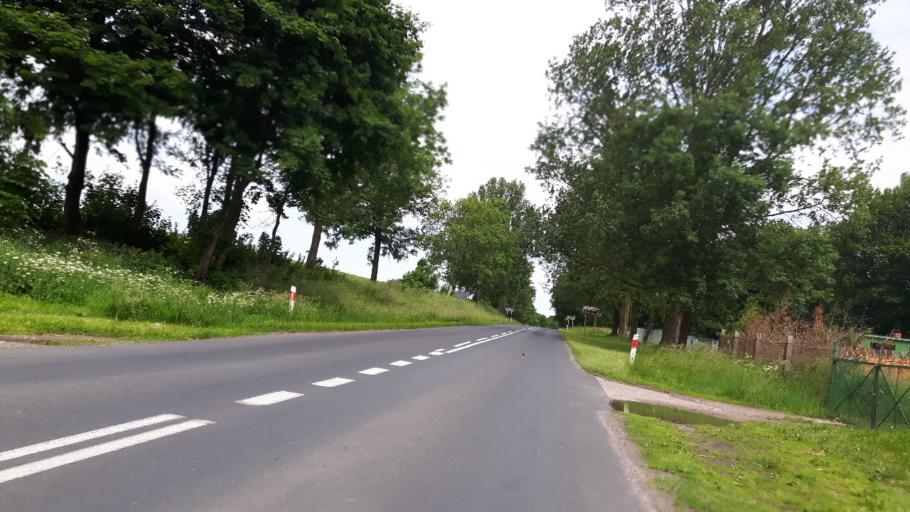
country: PL
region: West Pomeranian Voivodeship
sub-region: Powiat gryficki
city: Trzebiatow
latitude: 54.0158
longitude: 15.2431
